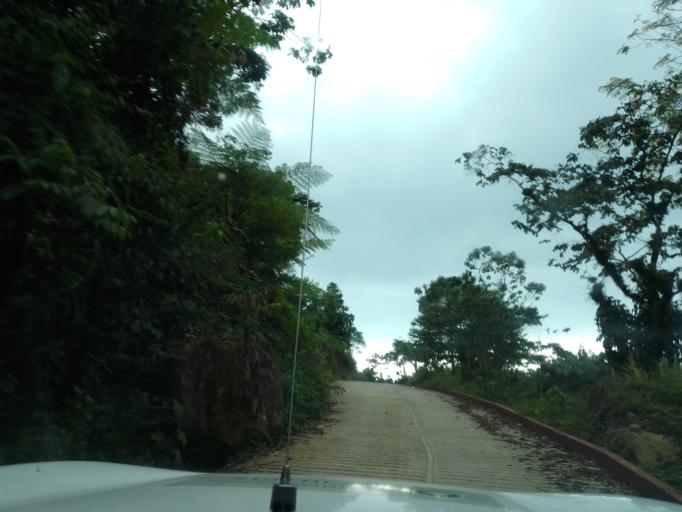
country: MX
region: Chiapas
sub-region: Union Juarez
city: Santo Domingo
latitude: 15.0694
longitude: -92.1159
